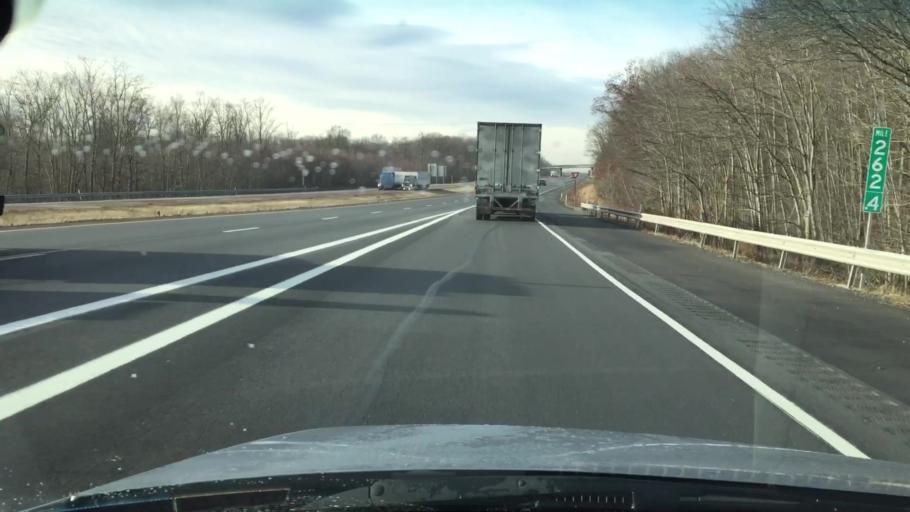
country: US
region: Pennsylvania
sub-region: Luzerne County
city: Harleigh
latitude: 41.0528
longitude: -75.9632
